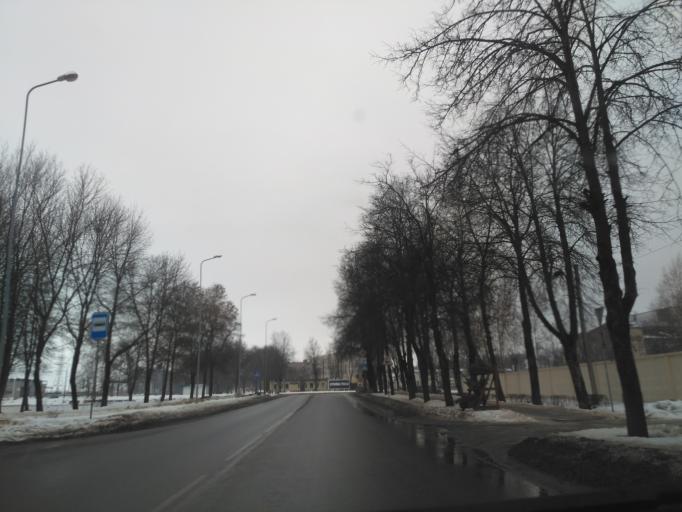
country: BY
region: Minsk
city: Horad Zhodzina
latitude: 54.0941
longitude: 28.3325
